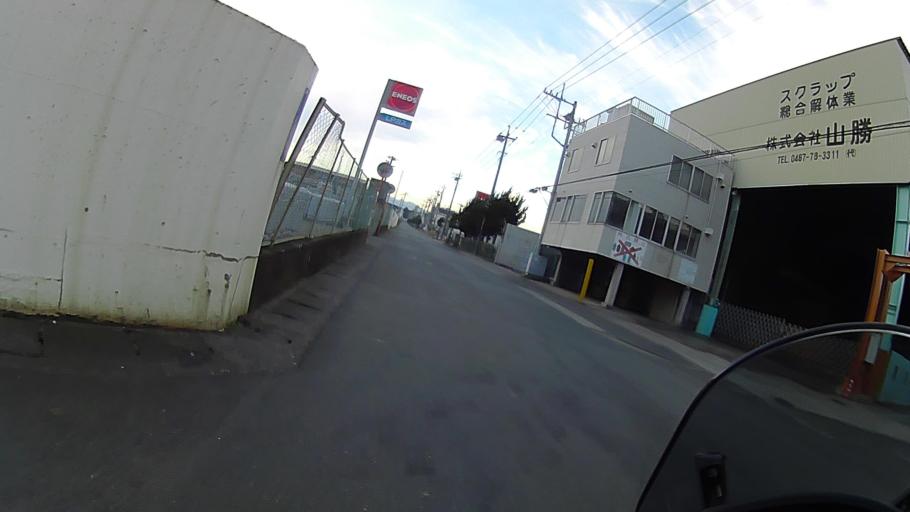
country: JP
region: Kanagawa
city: Minami-rinkan
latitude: 35.4244
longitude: 139.4260
